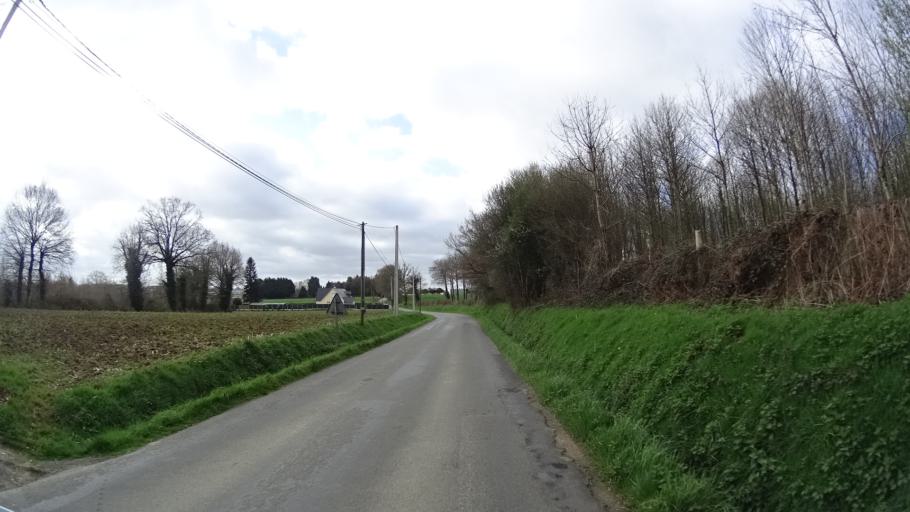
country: FR
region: Brittany
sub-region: Departement d'Ille-et-Vilaine
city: La Meziere
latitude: 48.2109
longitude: -1.7307
